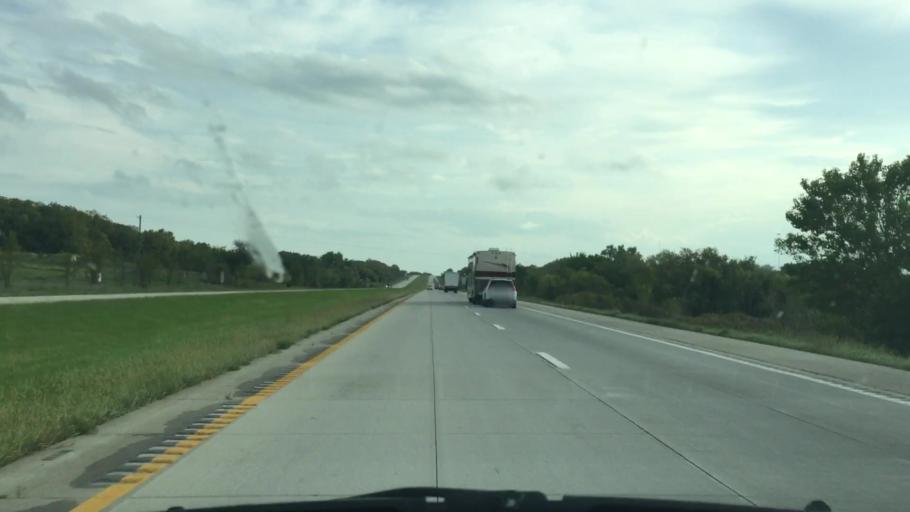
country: US
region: Missouri
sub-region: Daviess County
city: Gallatin
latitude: 39.9903
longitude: -94.0954
